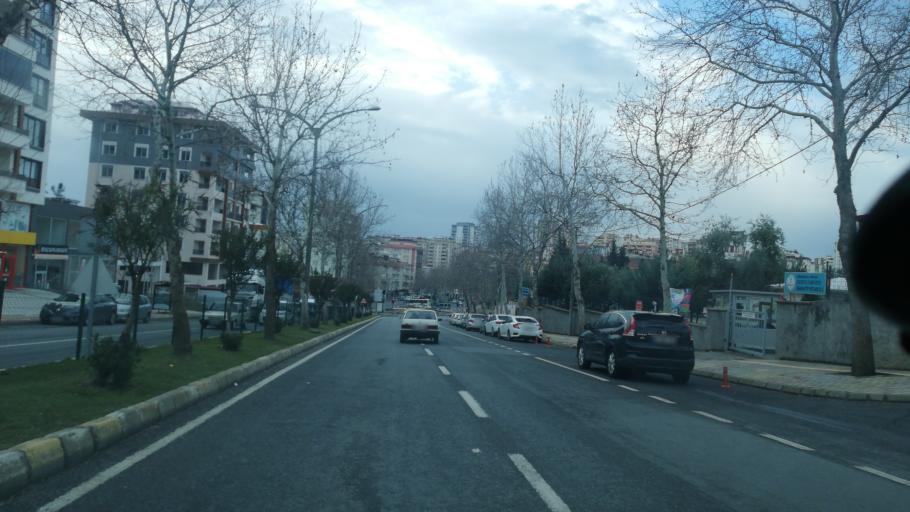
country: TR
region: Kahramanmaras
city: Kahramanmaras
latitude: 37.5882
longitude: 36.9034
